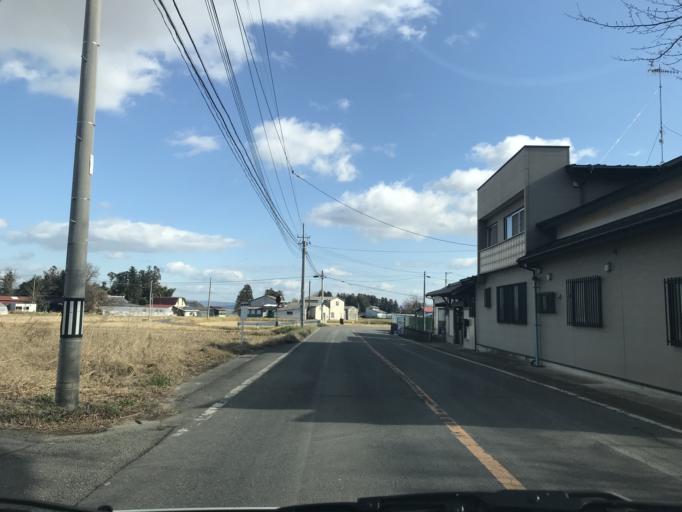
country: JP
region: Miyagi
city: Kogota
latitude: 38.7188
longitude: 141.0753
